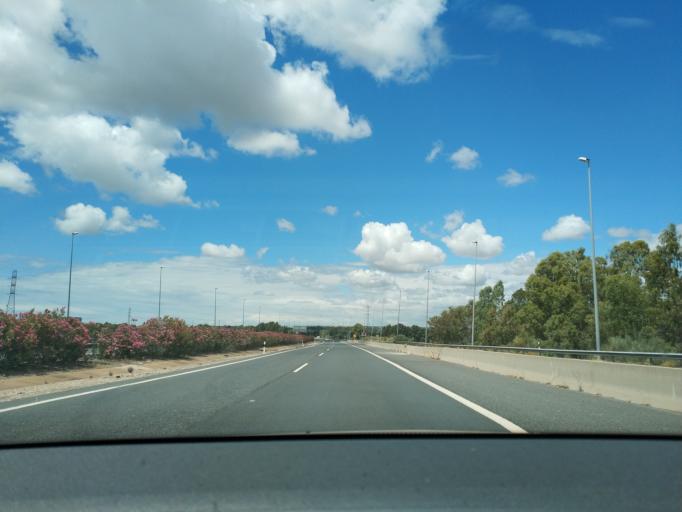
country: ES
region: Andalusia
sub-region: Provincia de Huelva
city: Gibraleon
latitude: 37.3562
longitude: -6.9617
